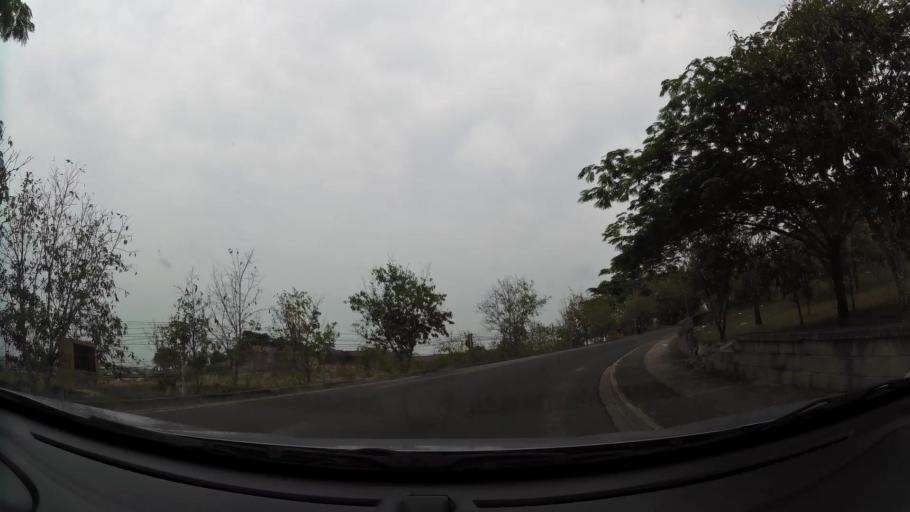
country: HN
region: Francisco Morazan
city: Yaguacire
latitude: 14.0458
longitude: -87.2233
